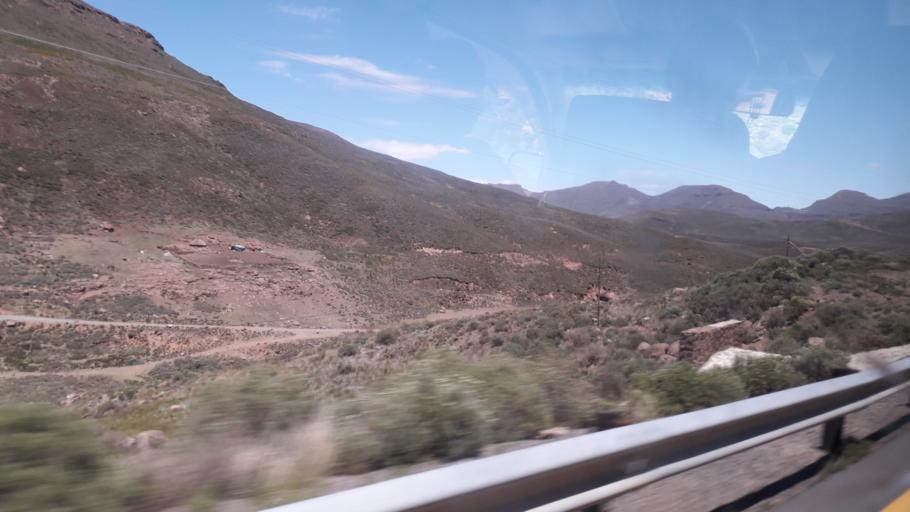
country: ZA
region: Orange Free State
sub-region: Thabo Mofutsanyana District Municipality
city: Phuthaditjhaba
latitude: -28.7681
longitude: 28.6627
